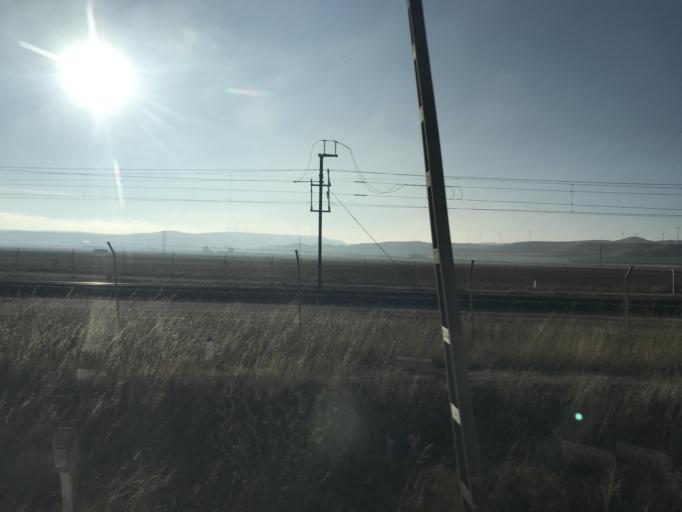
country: ES
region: Castille and Leon
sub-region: Provincia de Palencia
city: Herrera de Valdecanas
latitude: 42.0613
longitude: -4.2277
